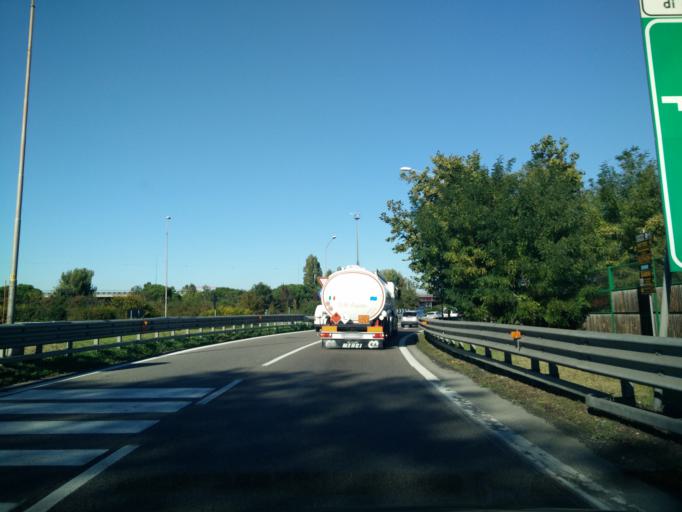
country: IT
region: Veneto
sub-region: Provincia di Venezia
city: Mestre
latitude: 45.4729
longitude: 12.2132
